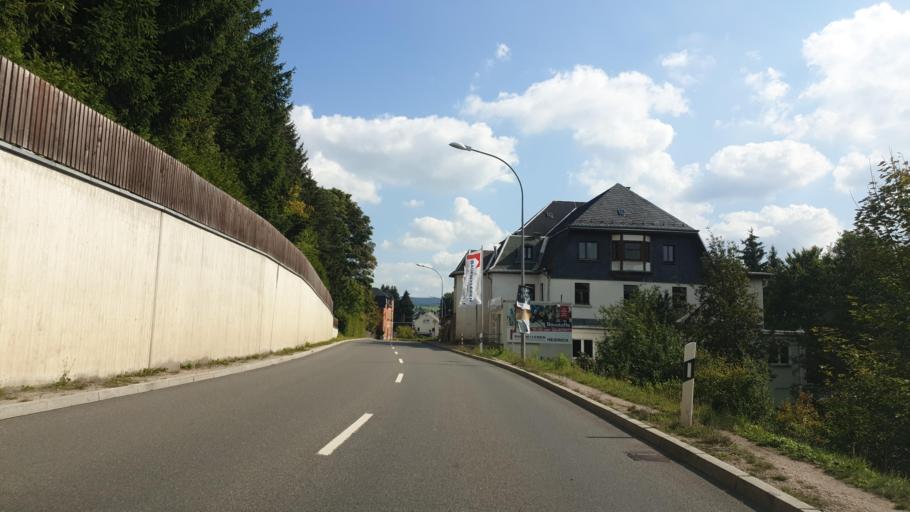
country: DE
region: Saxony
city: Rodewisch
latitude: 50.5326
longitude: 12.4072
